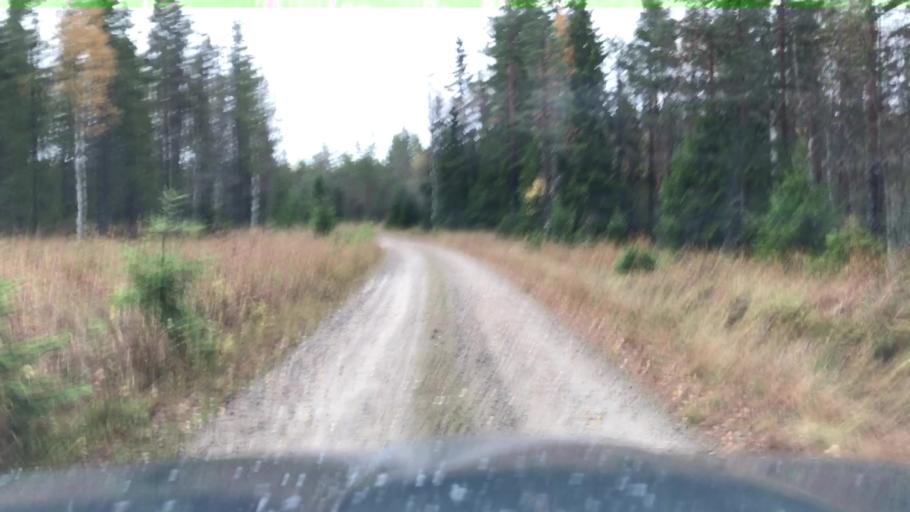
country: NO
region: Hedmark
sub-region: Trysil
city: Innbygda
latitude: 60.9238
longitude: 12.6246
